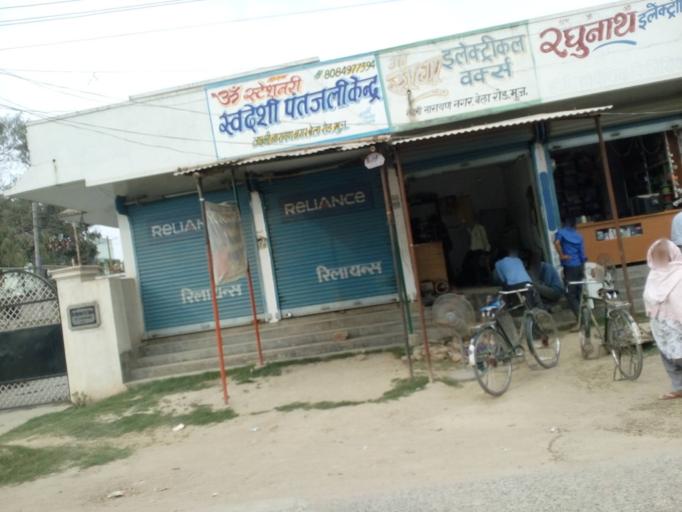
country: IN
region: Bihar
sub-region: Muzaffarpur
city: Muzaffarpur
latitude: 26.1019
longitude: 85.4068
